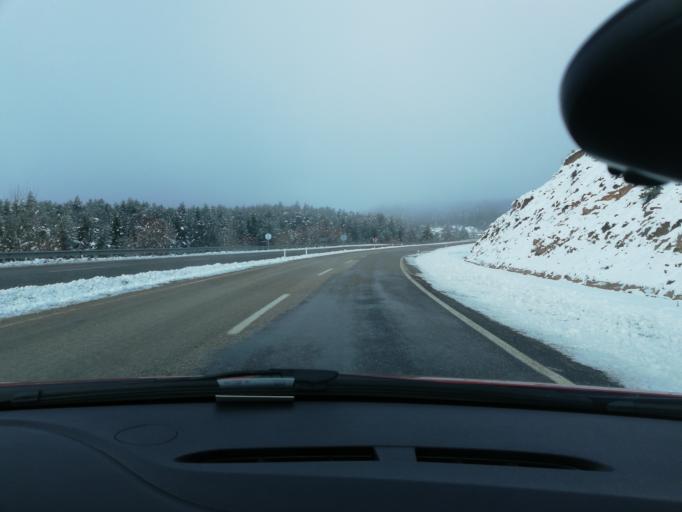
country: TR
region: Kastamonu
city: Ihsangazi
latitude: 41.2995
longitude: 33.5377
